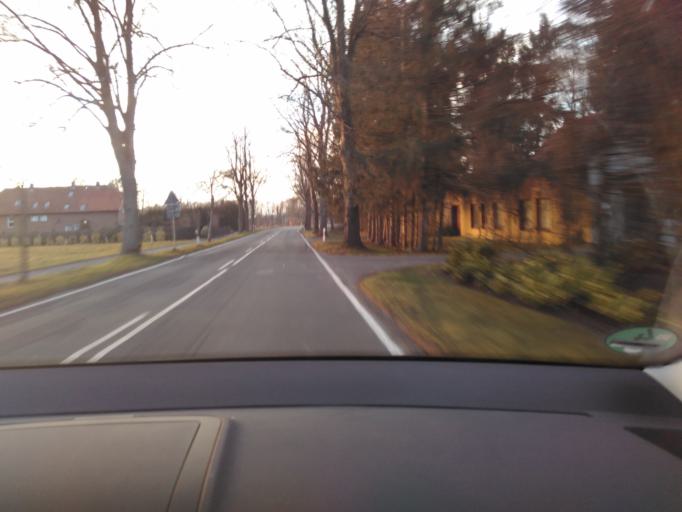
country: DE
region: North Rhine-Westphalia
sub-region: Regierungsbezirk Detmold
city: Verl
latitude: 51.9078
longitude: 8.4922
